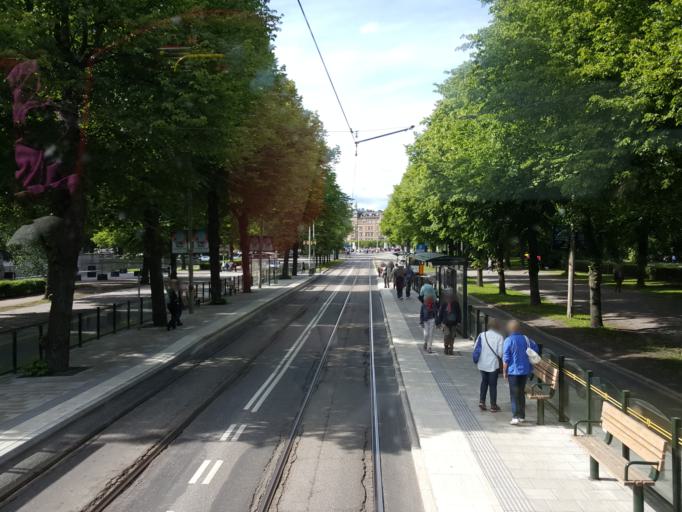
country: SE
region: Stockholm
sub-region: Stockholms Kommun
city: OEstermalm
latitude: 59.3288
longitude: 18.0960
